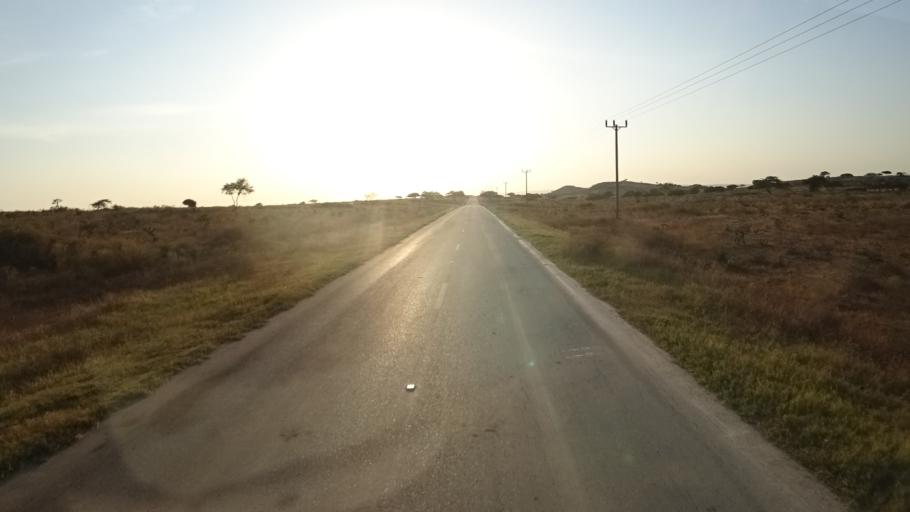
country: OM
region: Zufar
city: Salalah
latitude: 17.1475
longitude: 54.6146
